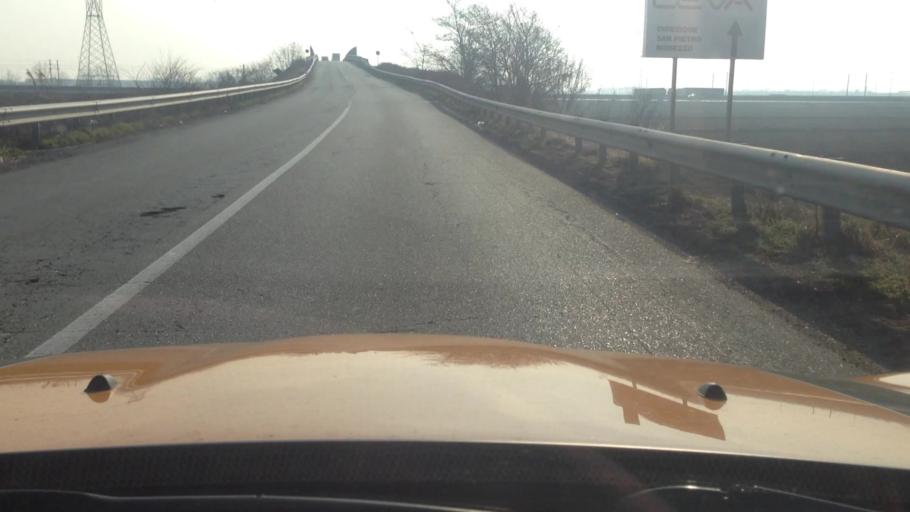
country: IT
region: Piedmont
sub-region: Provincia di Novara
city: San Pietro Mosezzo
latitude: 45.4760
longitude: 8.5575
